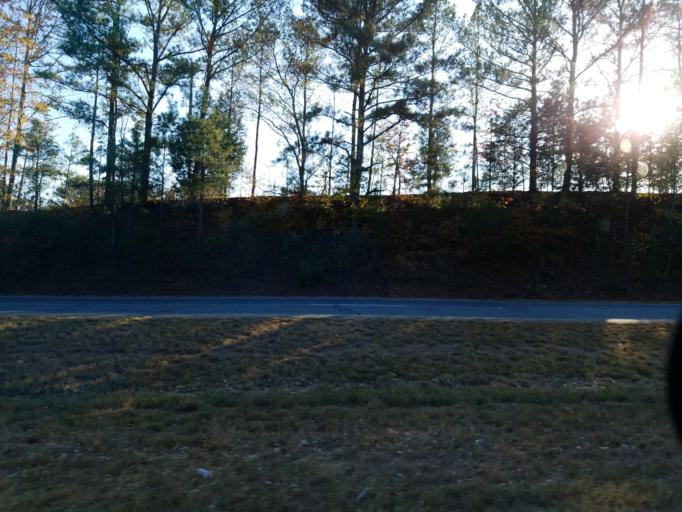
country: US
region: Georgia
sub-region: Bartow County
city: Euharlee
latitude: 34.2215
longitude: -84.8816
